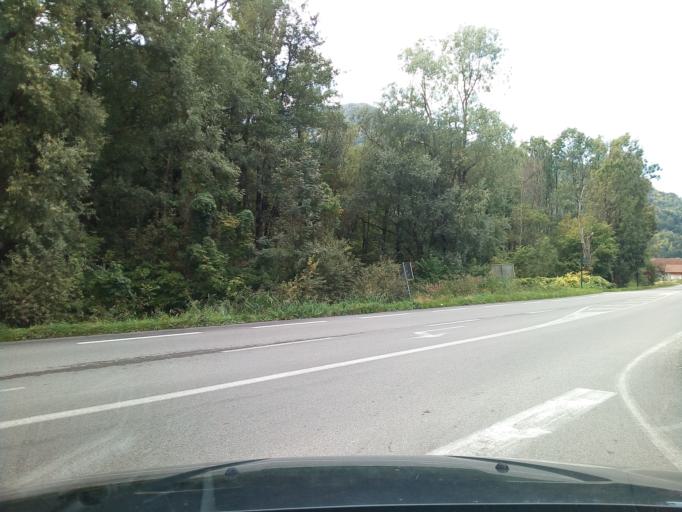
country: FR
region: Rhone-Alpes
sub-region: Departement de l'Isere
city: Le Cheylas
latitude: 45.3674
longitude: 6.0370
